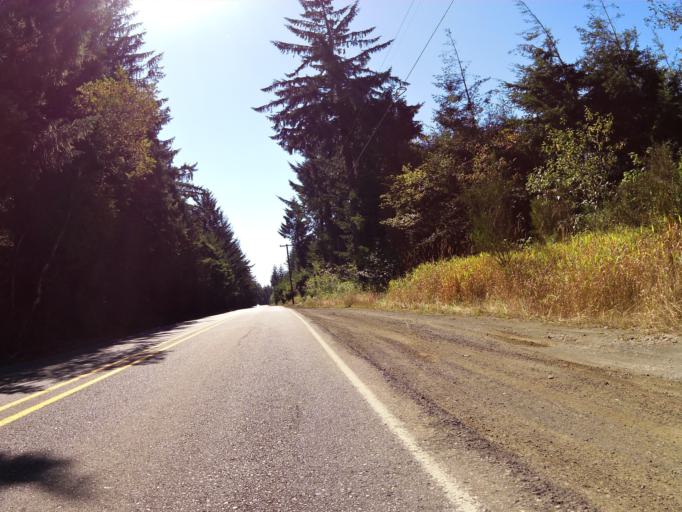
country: US
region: Oregon
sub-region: Coos County
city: Barview
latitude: 43.3228
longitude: -124.3418
